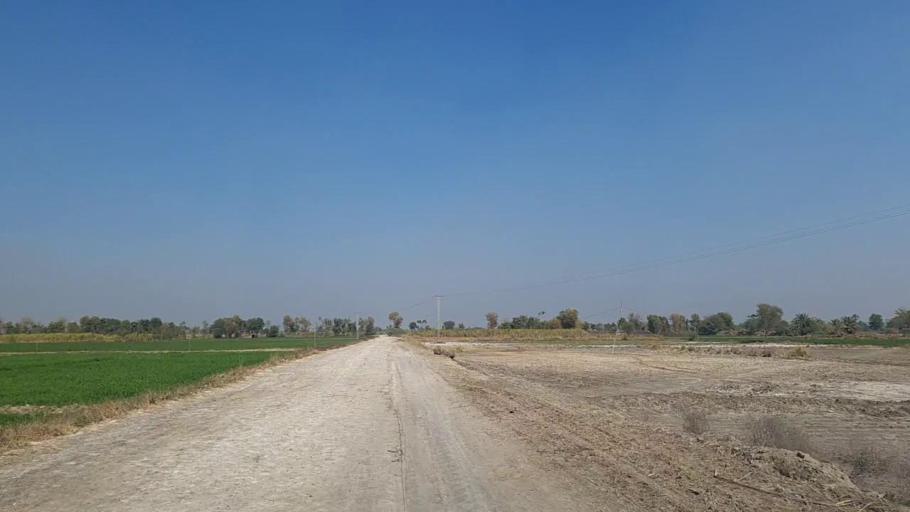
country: PK
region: Sindh
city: Daur
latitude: 26.4858
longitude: 68.3384
